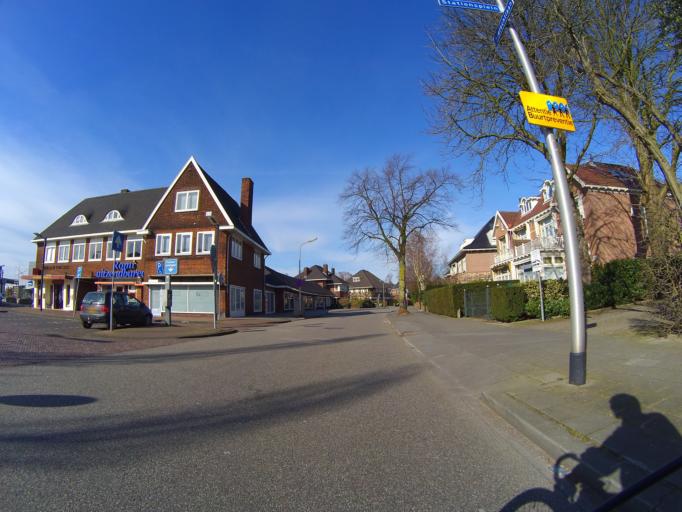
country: NL
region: North Holland
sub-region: Gemeente Bussum
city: Bussum
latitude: 52.2813
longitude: 5.1582
